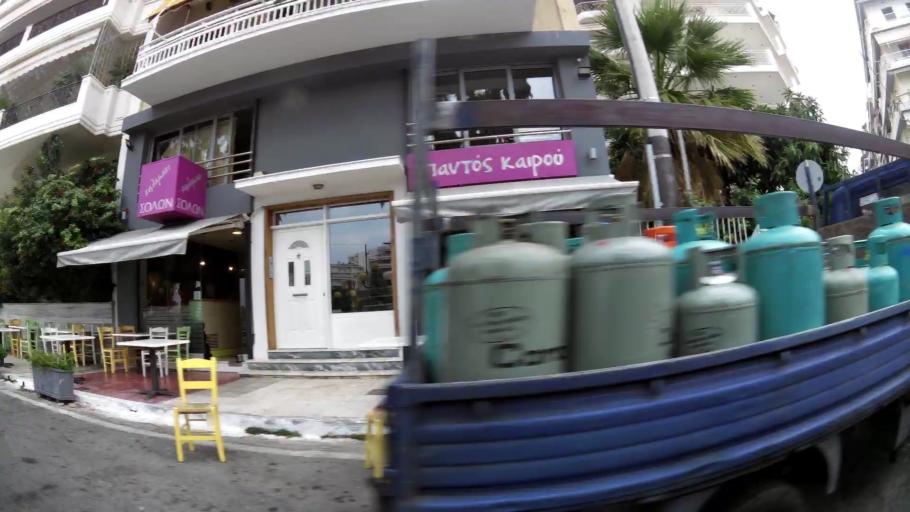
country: GR
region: Attica
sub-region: Nomos Attikis
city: Piraeus
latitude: 37.9293
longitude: 23.6299
